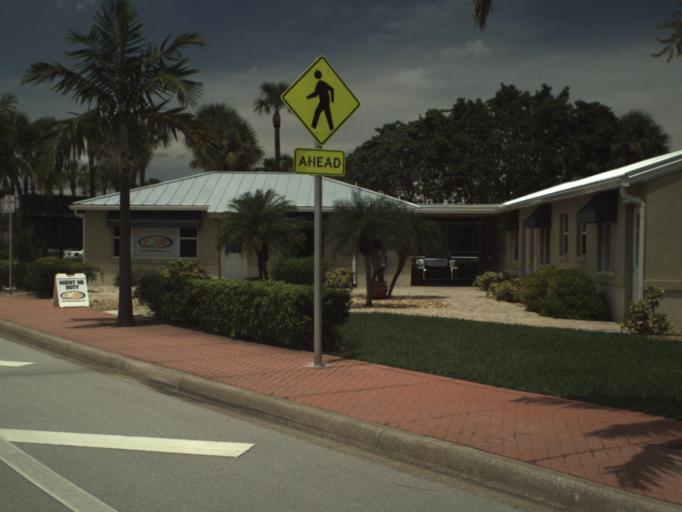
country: US
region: Florida
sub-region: Palm Beach County
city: Palm Beach Shores
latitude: 26.7841
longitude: -80.0357
